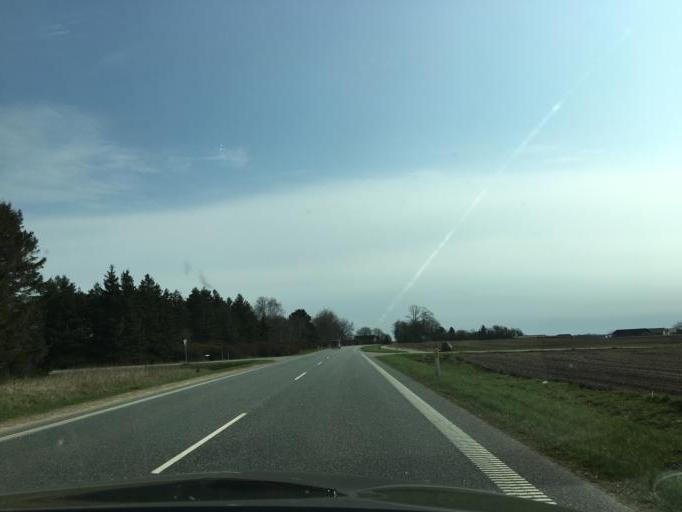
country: DK
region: South Denmark
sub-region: Kolding Kommune
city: Lunderskov
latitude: 55.4834
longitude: 9.2673
